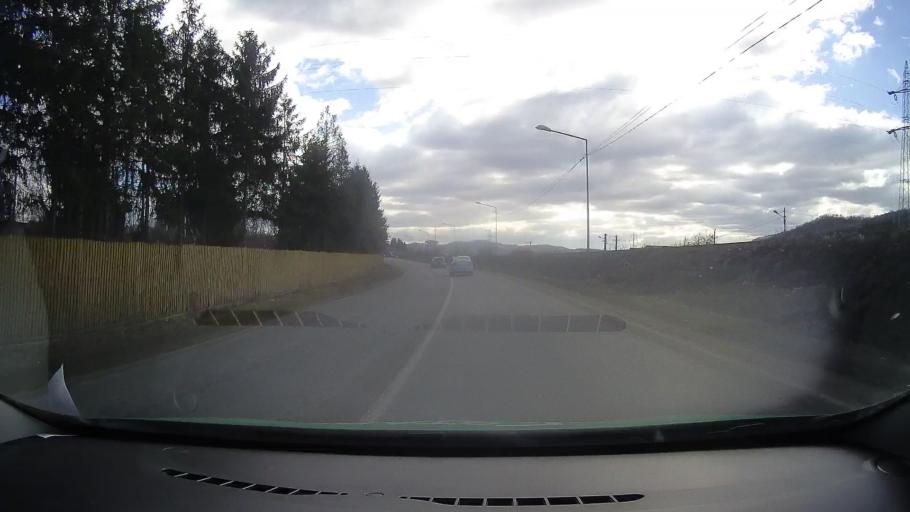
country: RO
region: Dambovita
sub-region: Oras Pucioasa
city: Pucioasa
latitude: 45.0838
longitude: 25.4218
